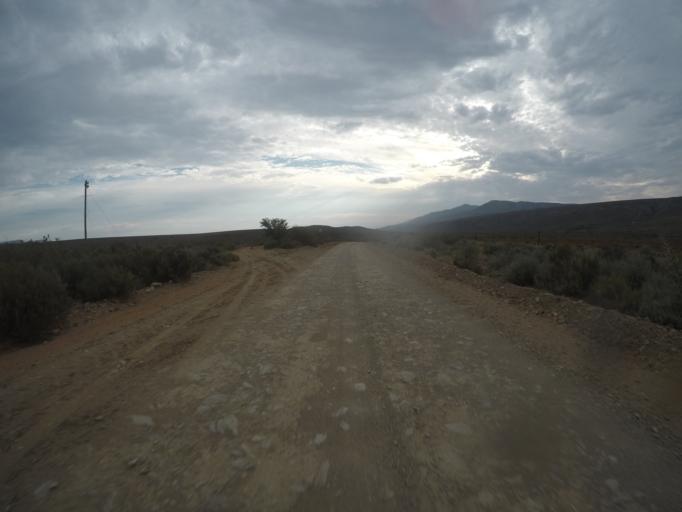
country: ZA
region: Eastern Cape
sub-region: Cacadu District Municipality
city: Willowmore
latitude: -33.4923
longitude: 23.5733
